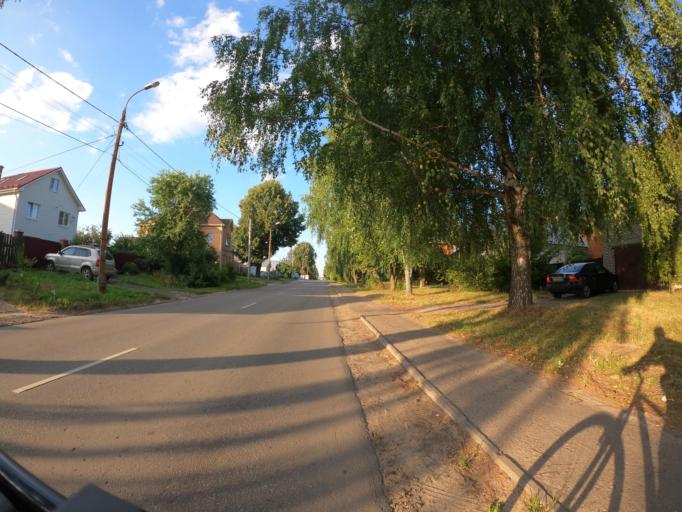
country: RU
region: Moskovskaya
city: Raduzhnyy
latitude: 55.1034
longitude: 38.7348
